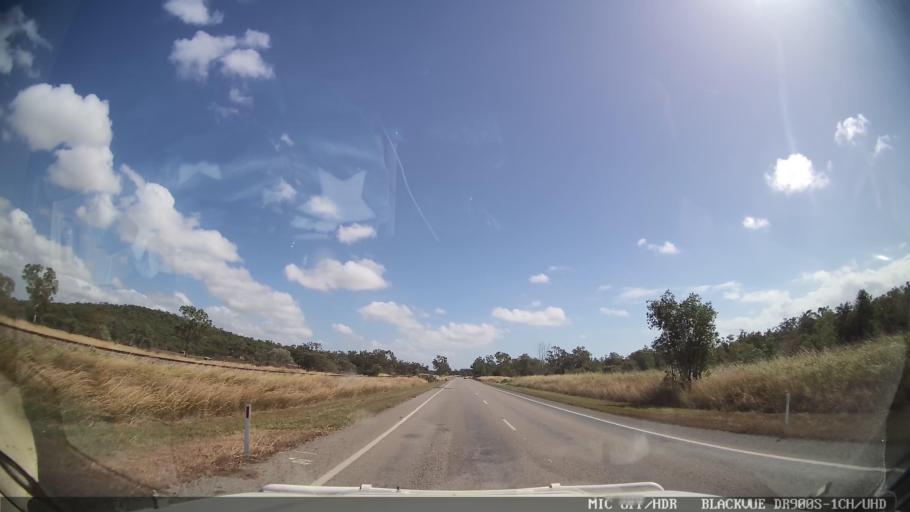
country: AU
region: Queensland
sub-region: Whitsunday
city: Bowen
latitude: -20.1815
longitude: 148.3515
